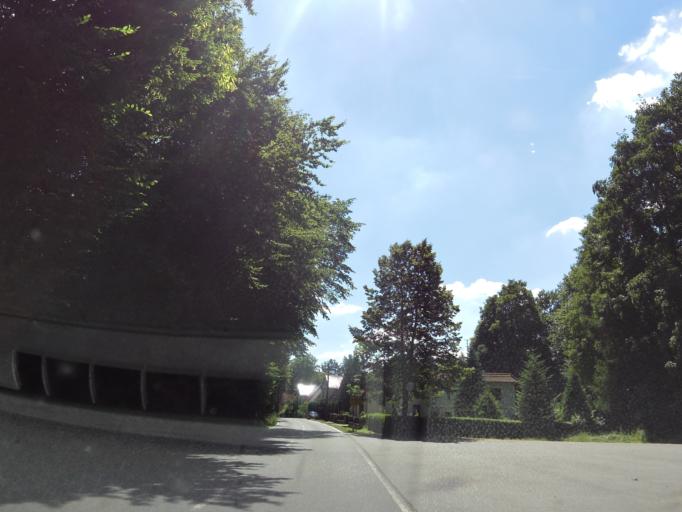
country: DE
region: Thuringia
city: Reichenbach
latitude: 50.8808
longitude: 11.8999
